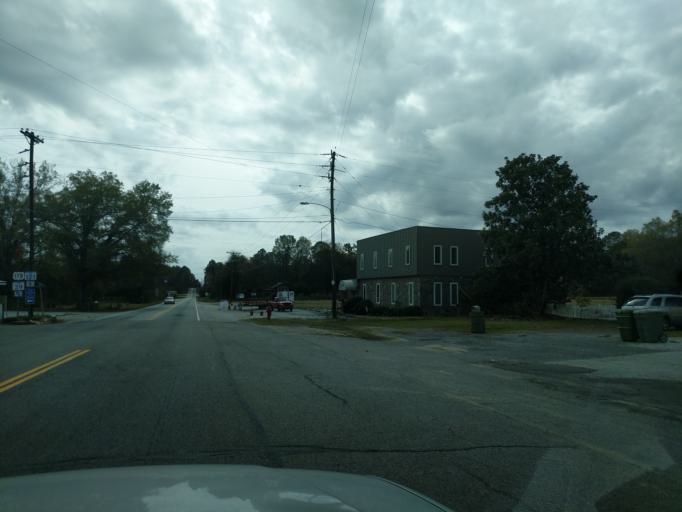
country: US
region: South Carolina
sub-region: Saluda County
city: Saluda
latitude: 33.9994
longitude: -81.7719
